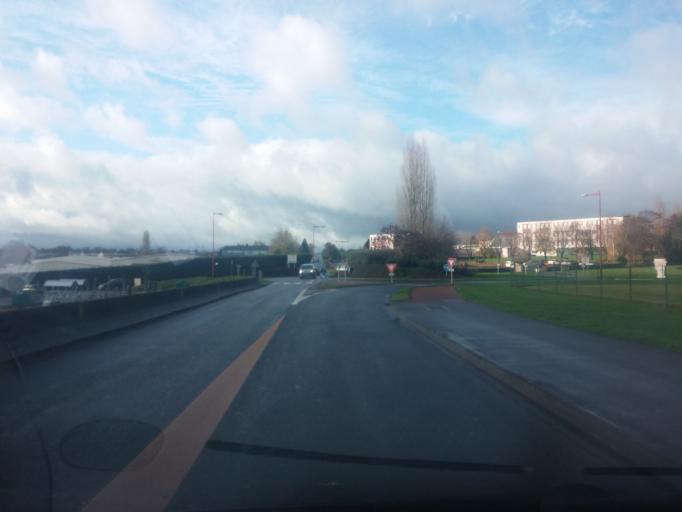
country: FR
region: Lower Normandy
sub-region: Departement du Calvados
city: Conde-sur-Noireau
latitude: 48.8520
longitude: -0.5681
